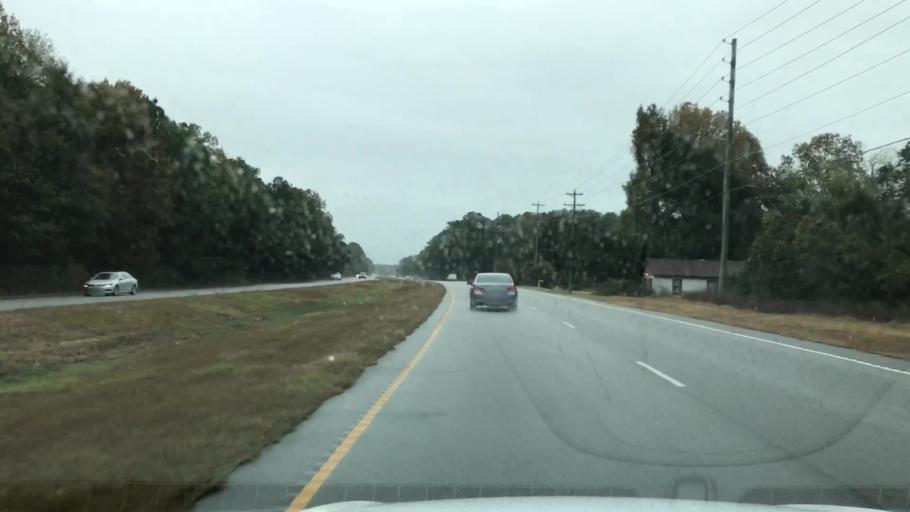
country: US
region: South Carolina
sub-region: Charleston County
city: Isle of Palms
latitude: 32.8886
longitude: -79.7423
